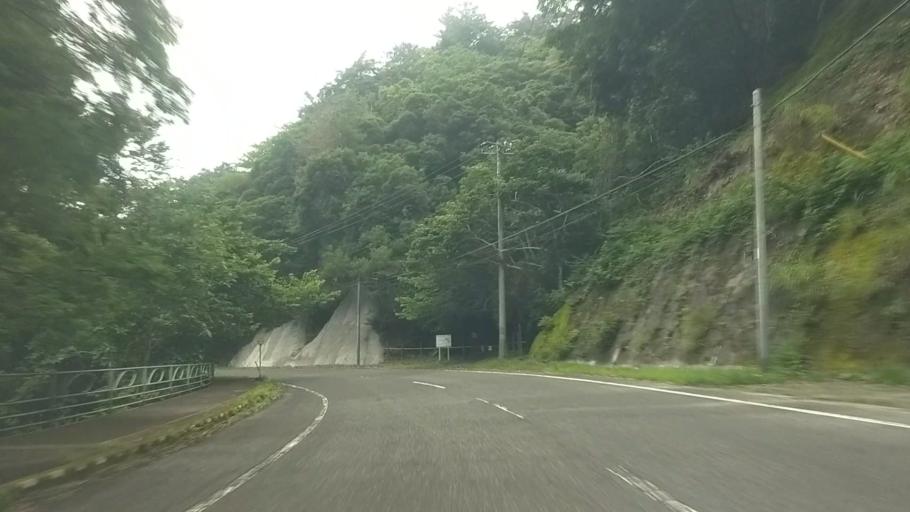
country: JP
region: Chiba
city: Kawaguchi
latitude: 35.1630
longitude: 140.1415
